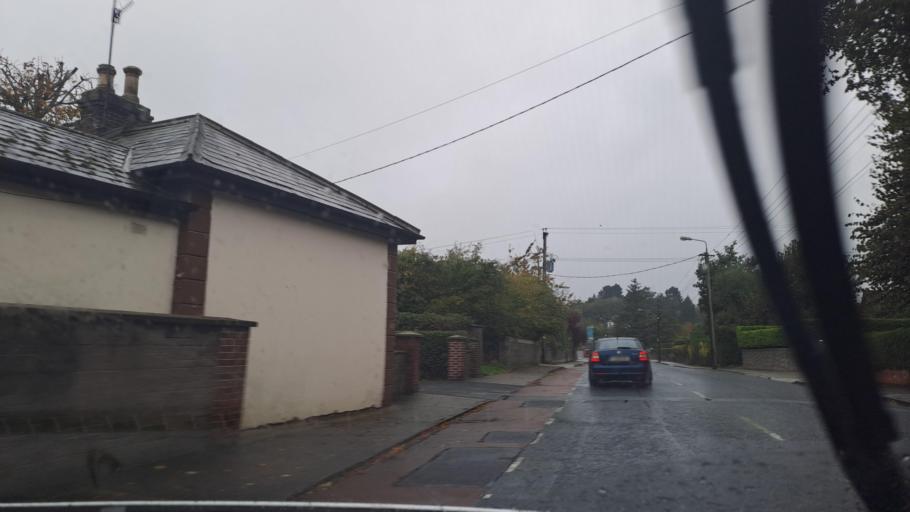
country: IE
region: Leinster
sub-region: Lu
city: Dundalk
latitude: 53.9999
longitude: -6.4198
